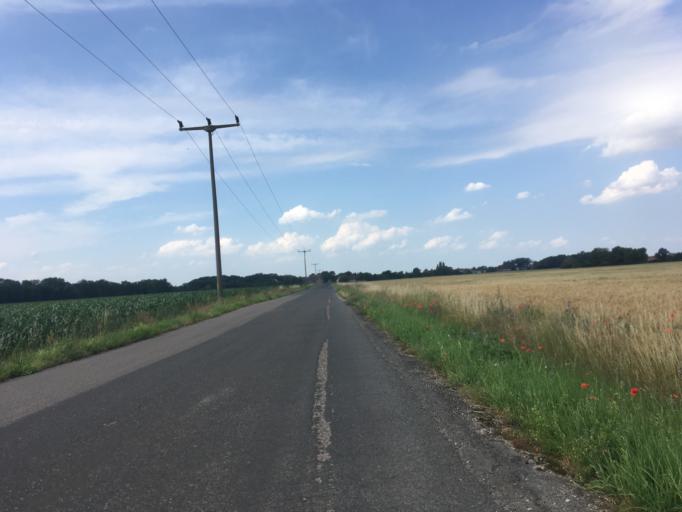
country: DE
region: Saxony-Anhalt
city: Quellendorf
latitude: 51.7738
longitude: 12.0913
